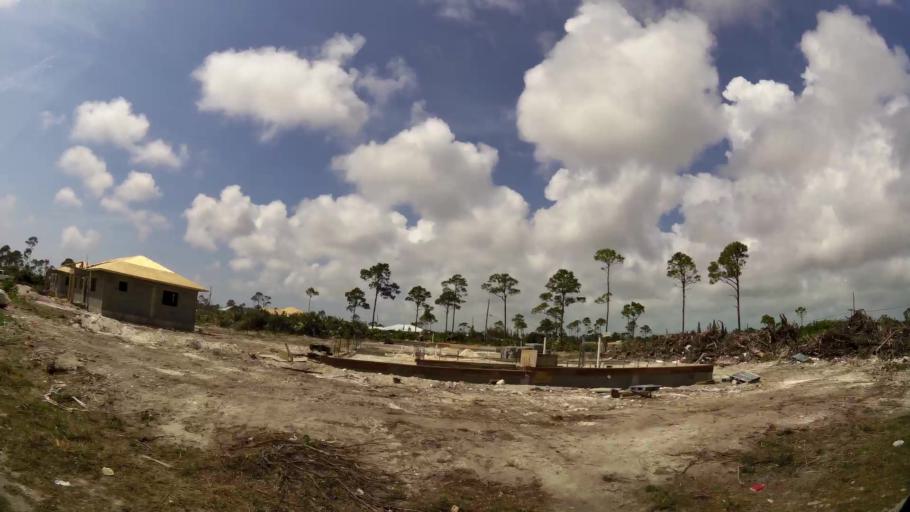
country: BS
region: Freeport
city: Freeport
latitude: 26.5142
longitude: -78.7185
